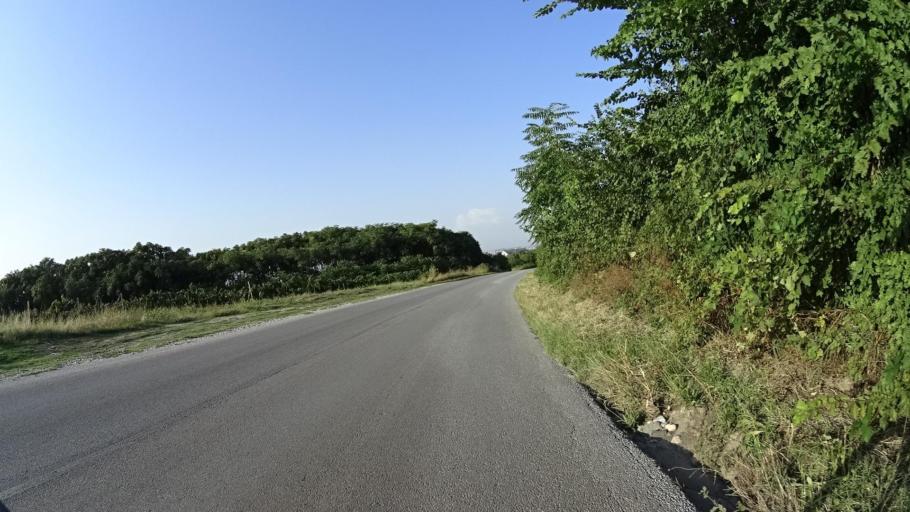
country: BG
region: Plovdiv
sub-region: Obshtina Plovdiv
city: Plovdiv
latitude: 42.0760
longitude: 24.7014
